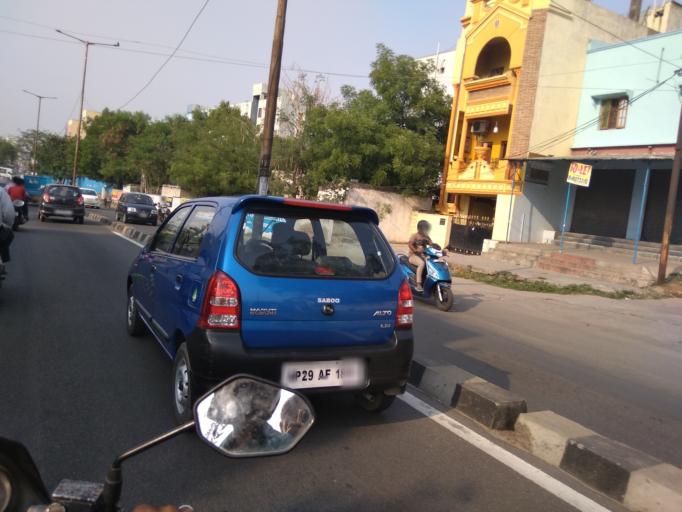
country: IN
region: Telangana
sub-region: Hyderabad
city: Malkajgiri
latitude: 17.4580
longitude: 78.5567
